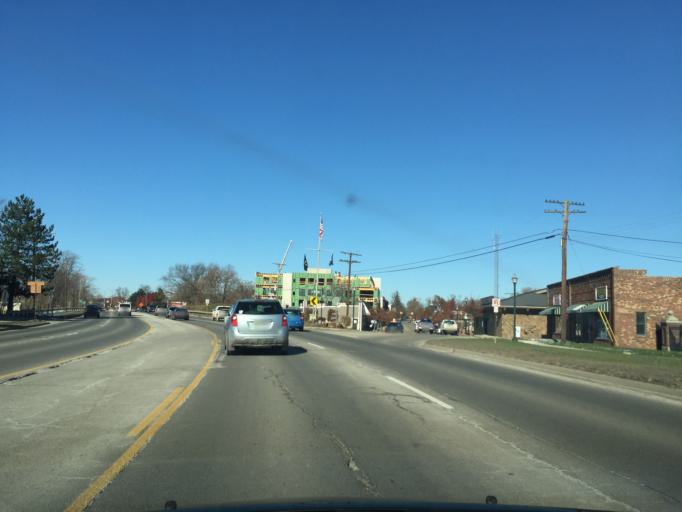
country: US
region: Michigan
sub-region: Oakland County
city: Lake Orion
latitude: 42.7816
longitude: -83.2397
